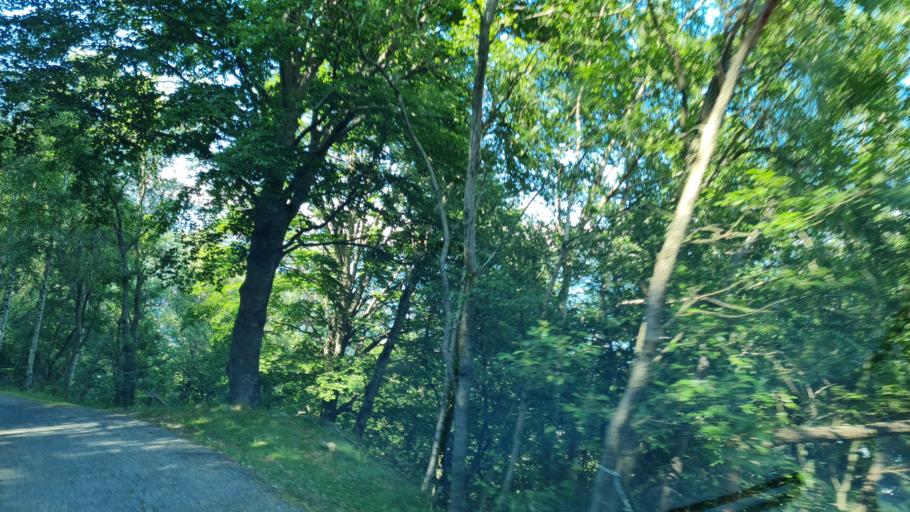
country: IT
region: Piedmont
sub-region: Provincia di Torino
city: Quincinetto
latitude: 45.5484
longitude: 7.7787
